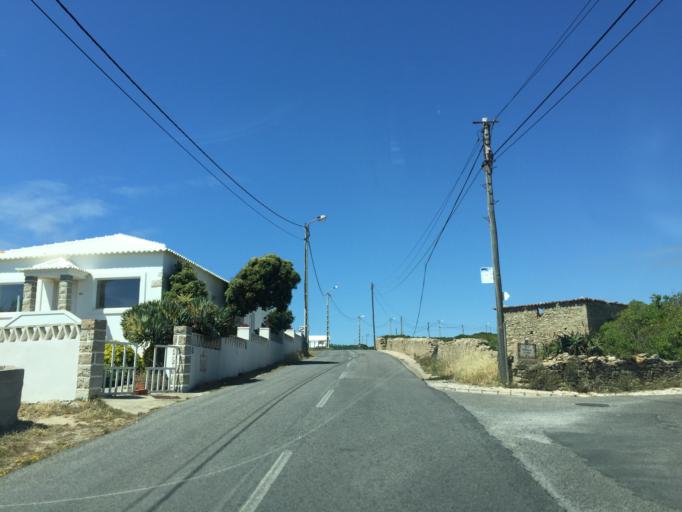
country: PT
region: Lisbon
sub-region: Sintra
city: Colares
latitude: 38.8420
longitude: -9.4608
